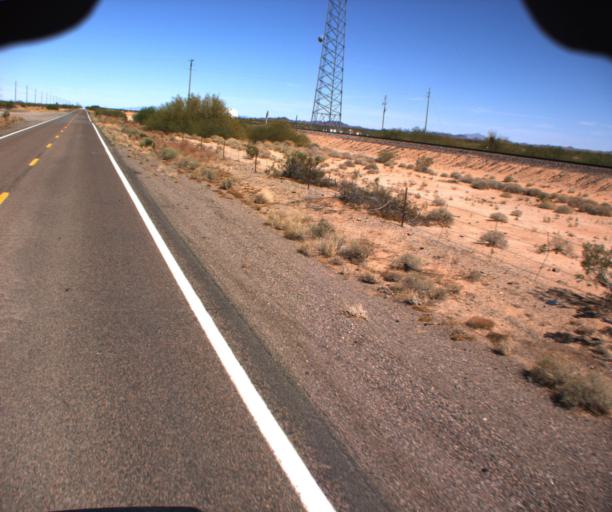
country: US
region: Arizona
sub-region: La Paz County
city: Salome
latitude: 33.8371
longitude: -113.8849
